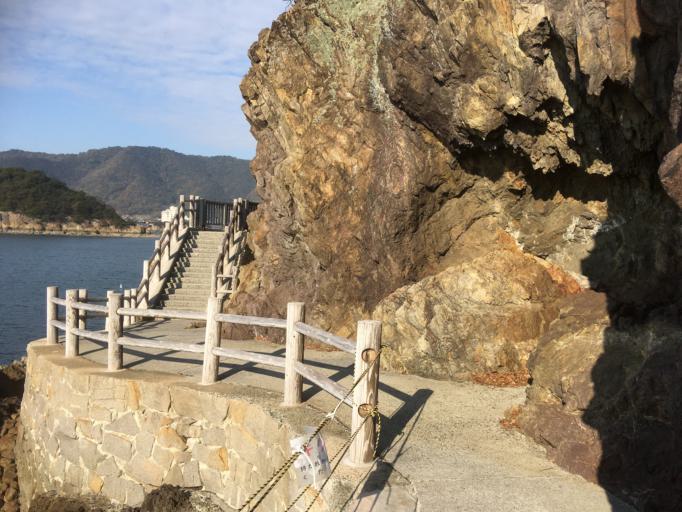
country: JP
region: Hiroshima
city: Fukuyama
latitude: 34.3808
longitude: 133.3943
